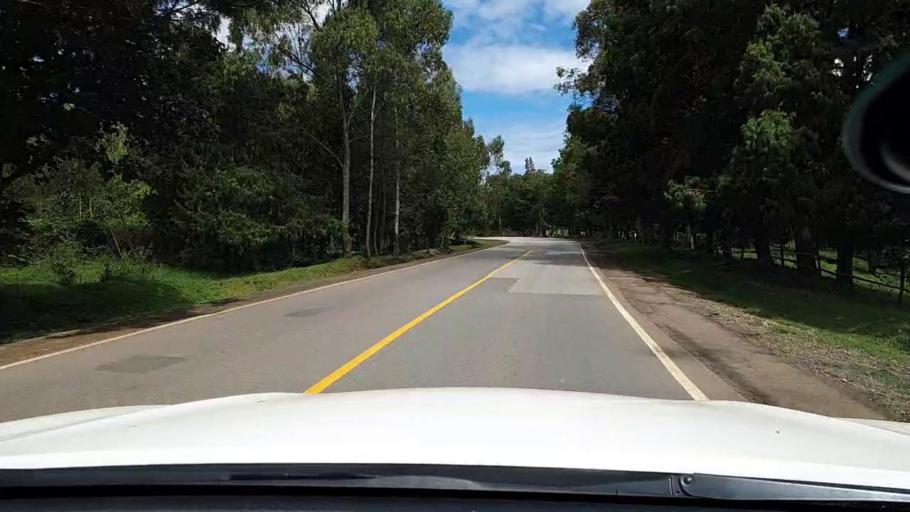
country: RW
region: Kigali
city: Kigali
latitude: -1.8224
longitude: 29.9420
